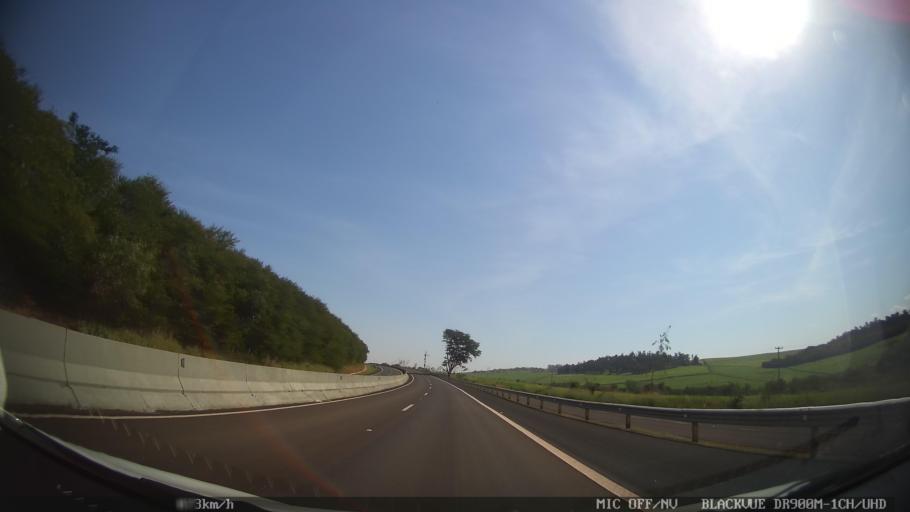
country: BR
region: Sao Paulo
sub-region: Ribeirao Preto
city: Ribeirao Preto
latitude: -21.1687
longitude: -47.8670
